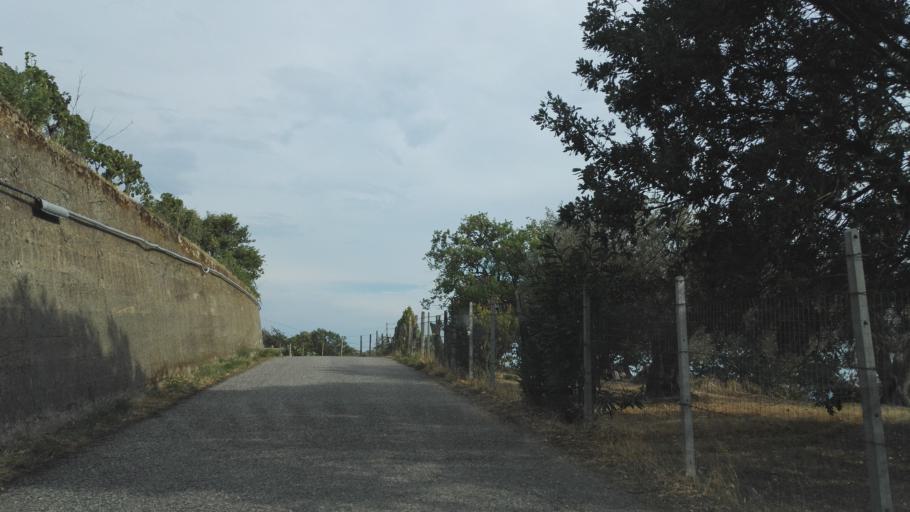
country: IT
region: Calabria
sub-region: Provincia di Reggio Calabria
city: Stignano
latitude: 38.4298
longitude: 16.4603
